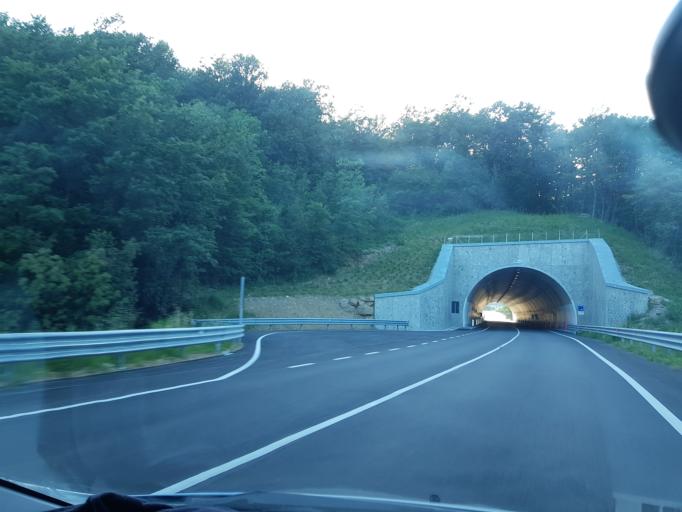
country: IT
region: Tuscany
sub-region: Provincia di Massa-Carrara
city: Fivizzano
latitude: 44.2007
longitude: 10.1026
